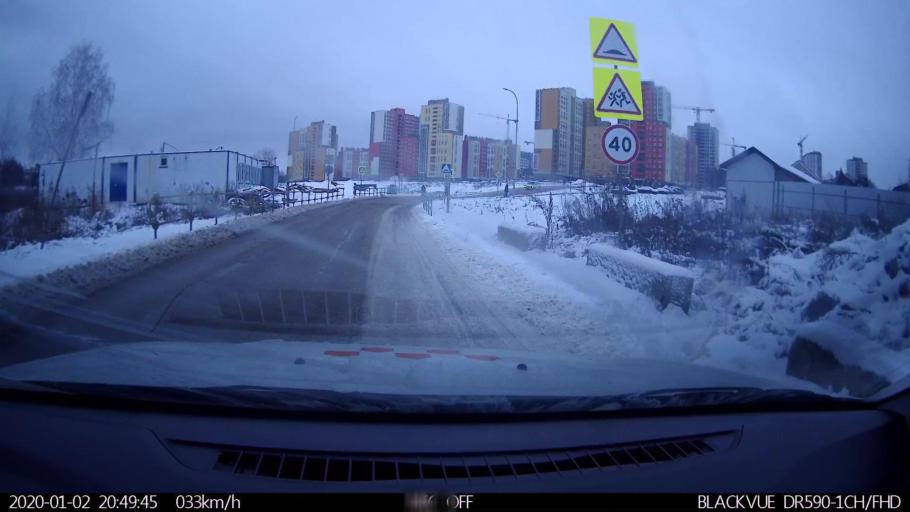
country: RU
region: Nizjnij Novgorod
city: Afonino
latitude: 56.2787
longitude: 44.0421
